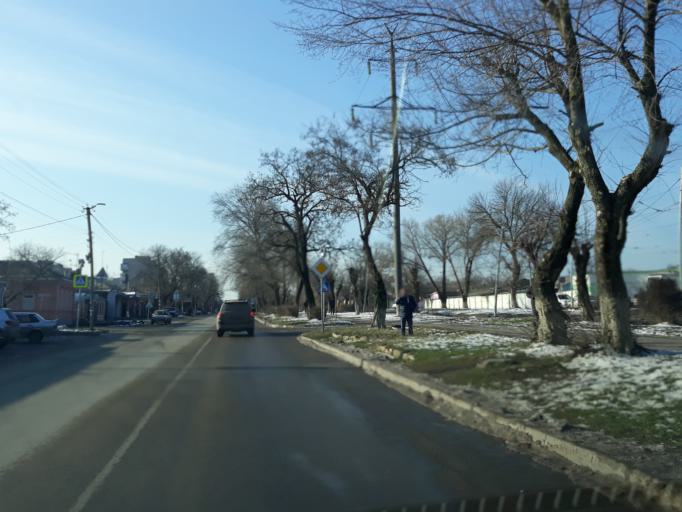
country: RU
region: Rostov
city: Taganrog
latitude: 47.2084
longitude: 38.9077
